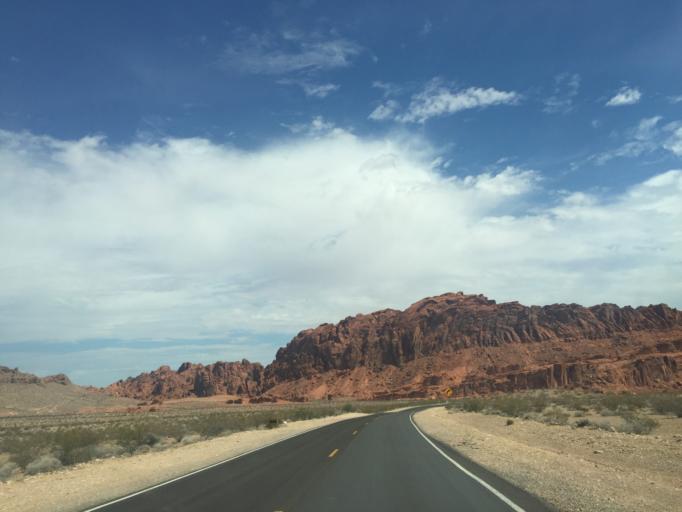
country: US
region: Nevada
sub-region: Clark County
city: Moapa Valley
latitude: 36.4241
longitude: -114.5425
